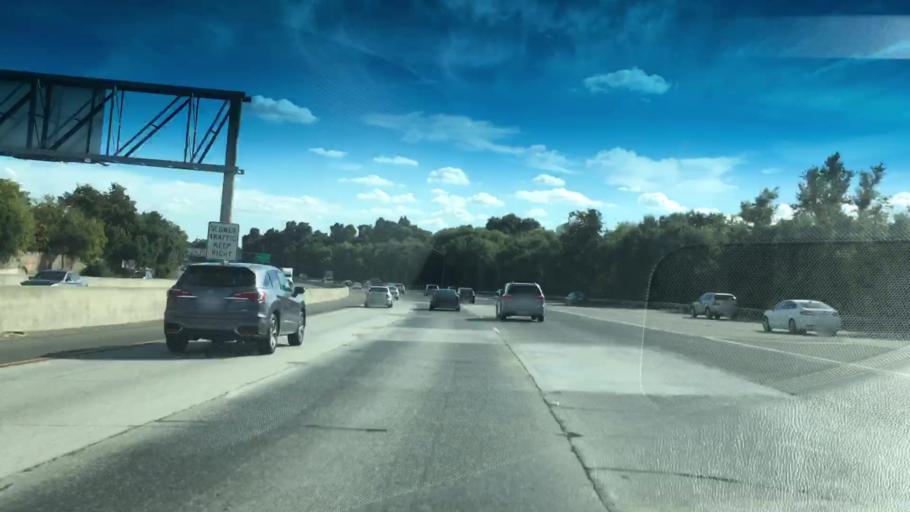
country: US
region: California
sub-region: Yolo County
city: West Sacramento
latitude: 38.5639
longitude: -121.5125
